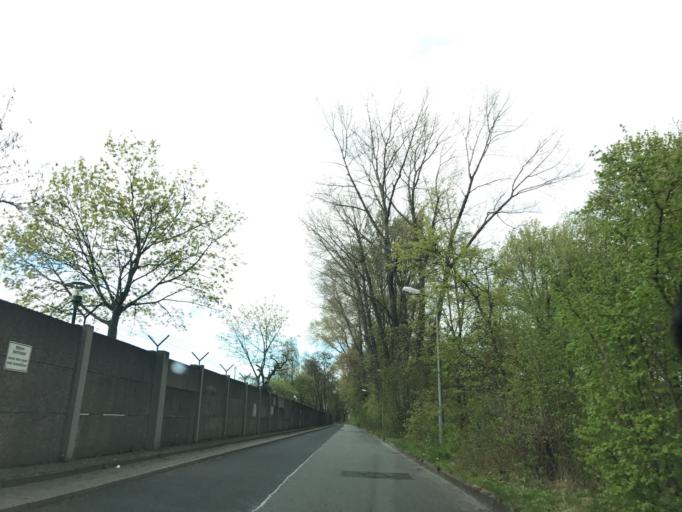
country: DE
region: Berlin
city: Reinickendorf
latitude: 52.5548
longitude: 13.3247
